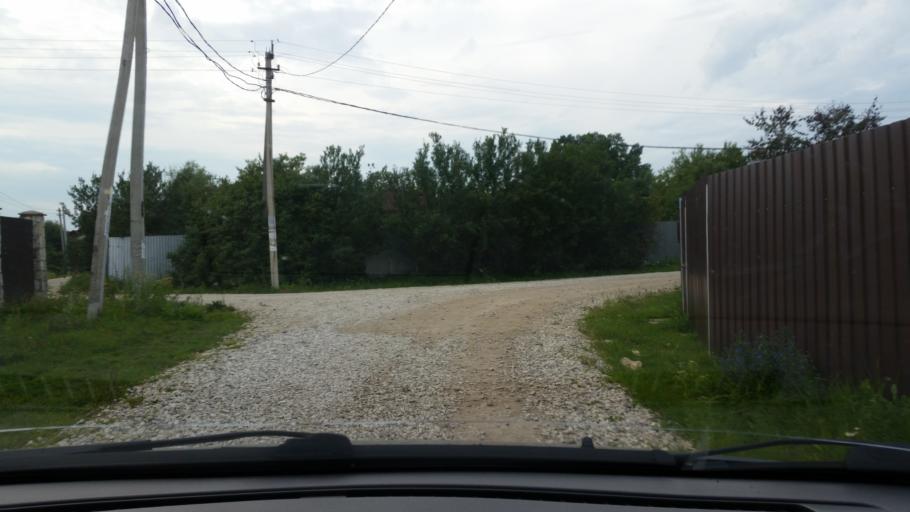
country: RU
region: Moskovskaya
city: Bol'shoye Gryzlovo
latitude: 54.8499
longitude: 37.7026
